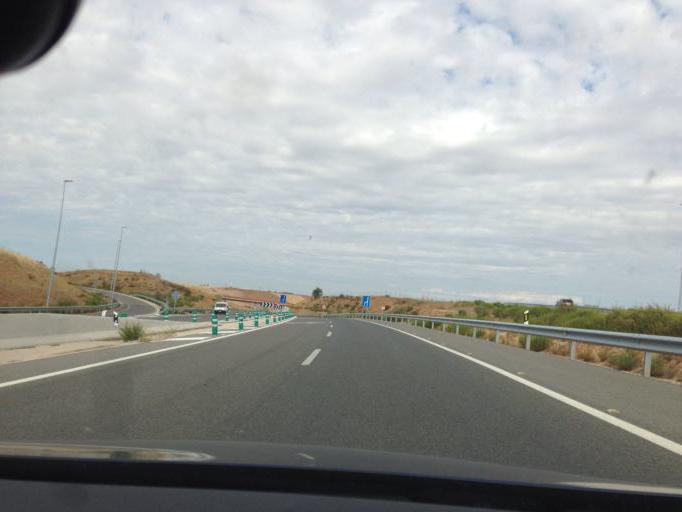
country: ES
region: Madrid
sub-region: Provincia de Madrid
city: Daganzo de Arriba
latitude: 40.5242
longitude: -3.4158
